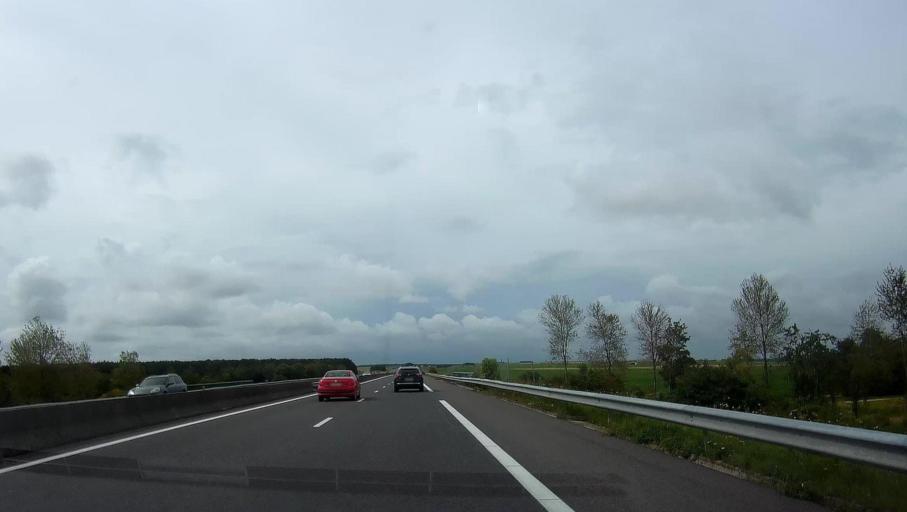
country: FR
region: Champagne-Ardenne
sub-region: Departement de l'Aube
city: Mailly-le-Camp
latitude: 48.7852
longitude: 4.2648
